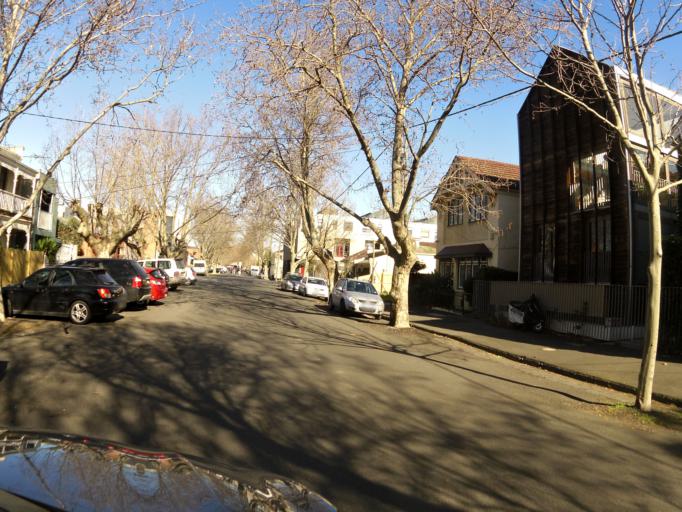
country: AU
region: Victoria
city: Abbotsford
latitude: -37.8064
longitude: 144.9951
